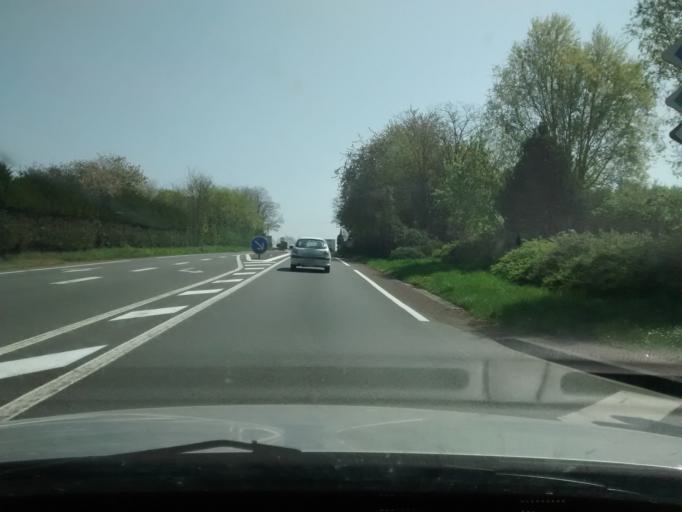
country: FR
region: Pays de la Loire
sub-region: Departement de la Sarthe
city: Trange
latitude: 48.0218
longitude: 0.1032
